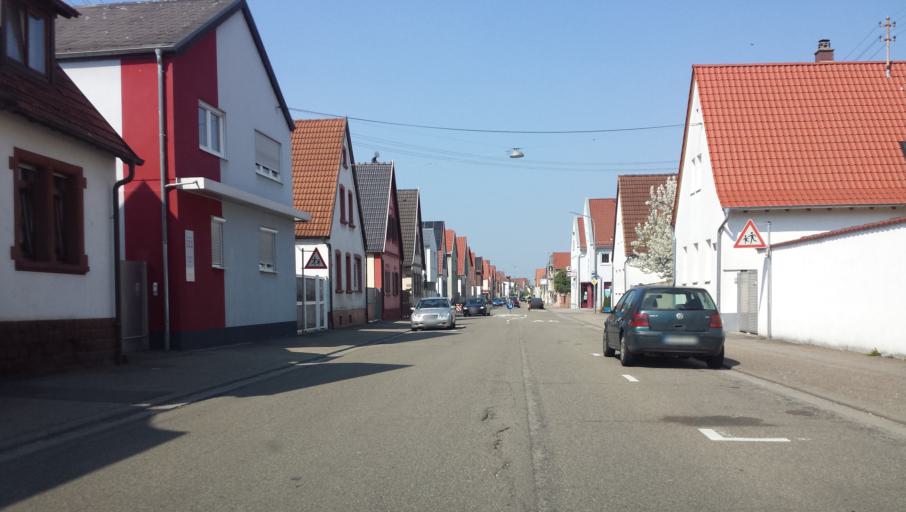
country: DE
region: Rheinland-Pfalz
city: Lingenfeld
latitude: 49.2447
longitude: 8.3448
